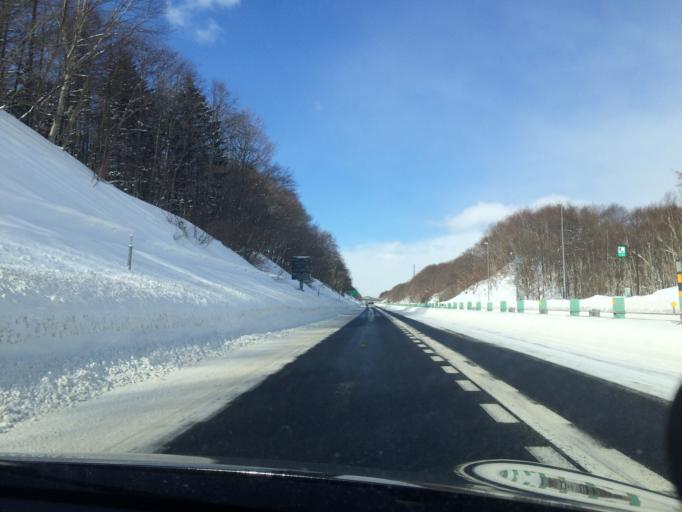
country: JP
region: Hokkaido
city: Kitahiroshima
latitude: 42.9260
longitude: 141.5383
